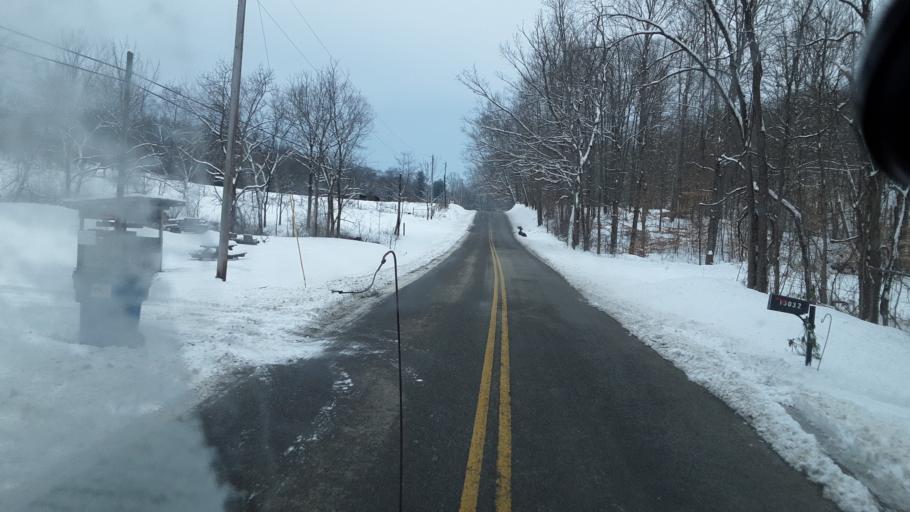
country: US
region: Ohio
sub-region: Perry County
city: Somerset
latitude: 39.9087
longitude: -82.2282
